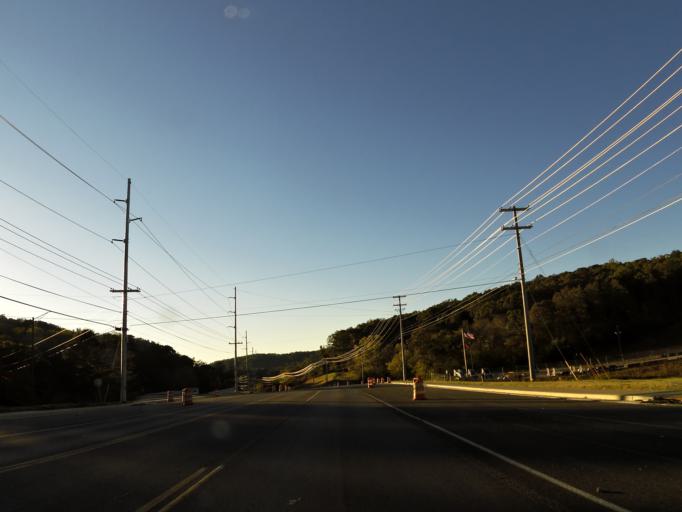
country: US
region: Tennessee
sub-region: Knox County
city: Knoxville
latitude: 35.9866
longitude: -84.0349
